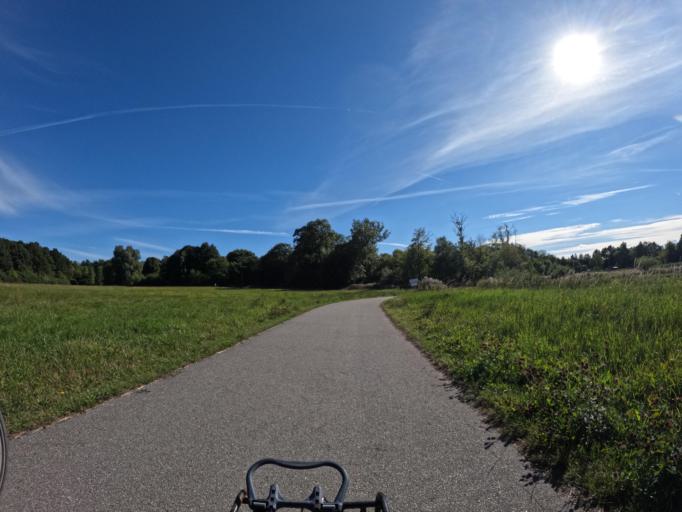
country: DK
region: Capital Region
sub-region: Hoje-Taastrup Kommune
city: Taastrup
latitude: 55.6621
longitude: 12.3236
